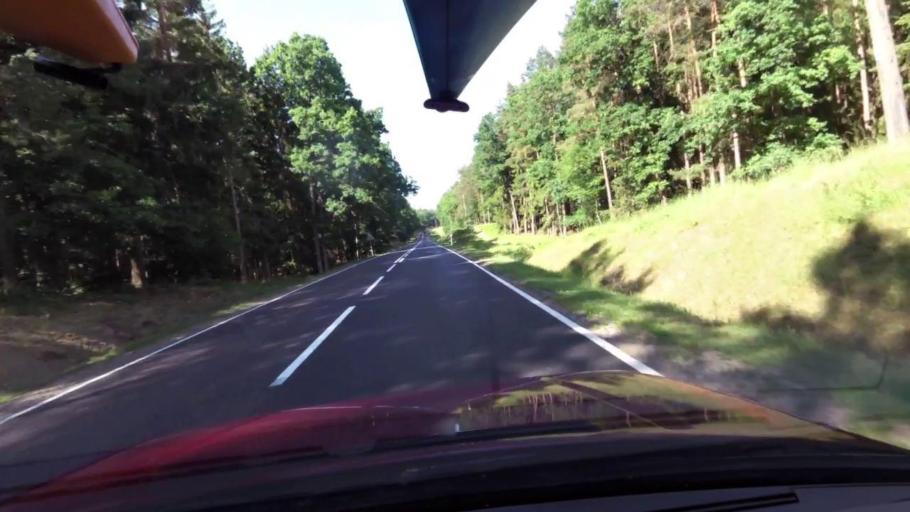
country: PL
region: Pomeranian Voivodeship
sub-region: Powiat bytowski
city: Trzebielino
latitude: 54.1232
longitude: 17.0050
